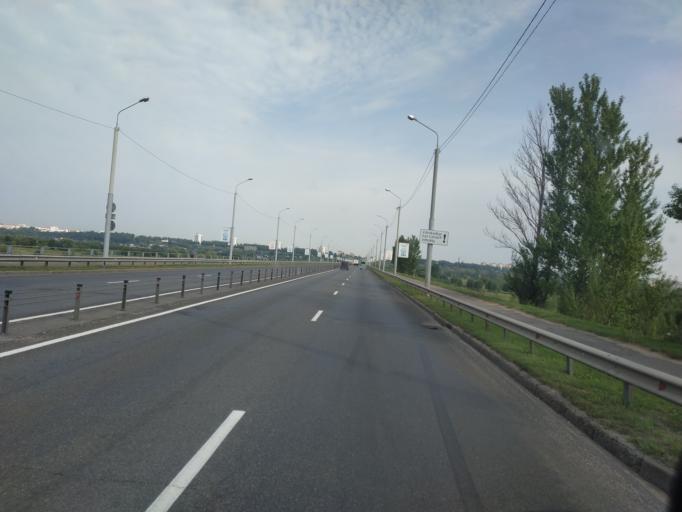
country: BY
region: Mogilev
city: Mahilyow
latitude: 53.8856
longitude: 30.3791
